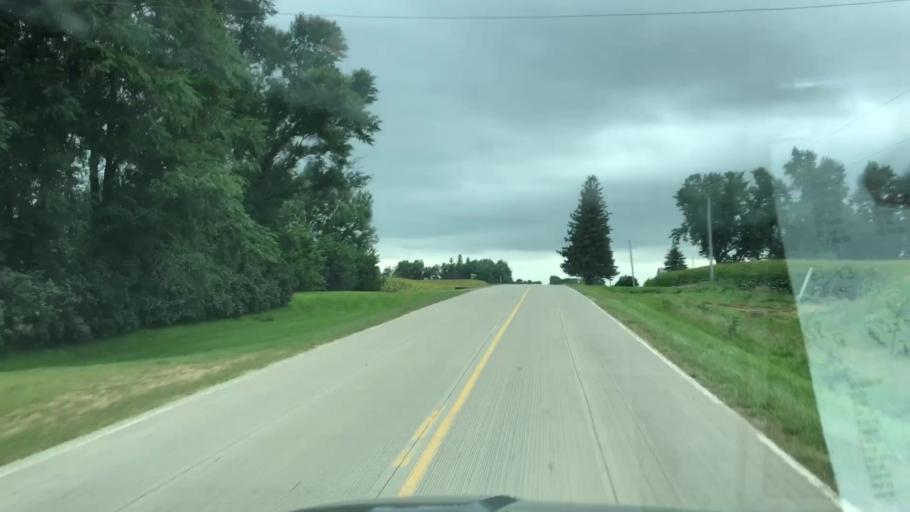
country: US
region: Iowa
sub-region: Sioux County
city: Alton
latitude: 43.1100
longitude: -95.9787
